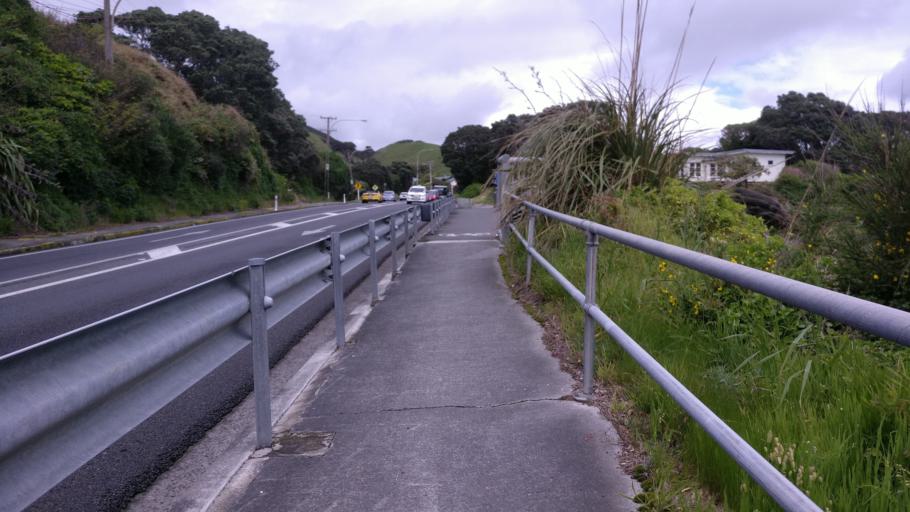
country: NZ
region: Wellington
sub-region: Porirua City
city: Porirua
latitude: -41.0307
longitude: 174.8969
